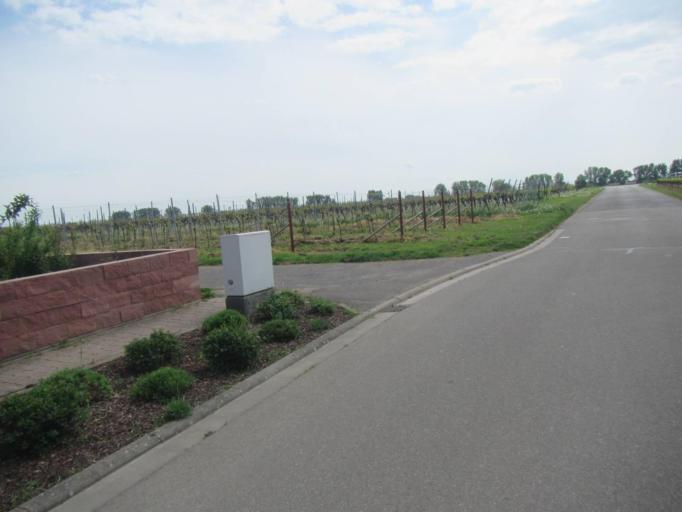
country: DE
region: Rheinland-Pfalz
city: Bobingen
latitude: 49.2685
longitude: 8.2278
